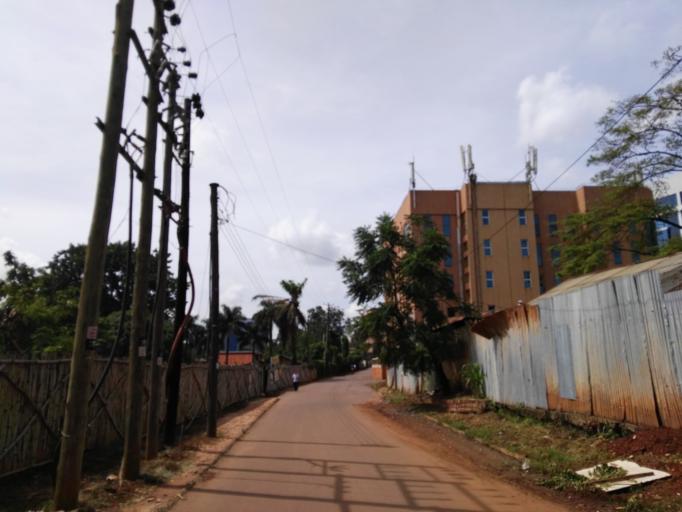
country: UG
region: Central Region
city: Kampala Central Division
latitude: 0.3207
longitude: 32.5763
